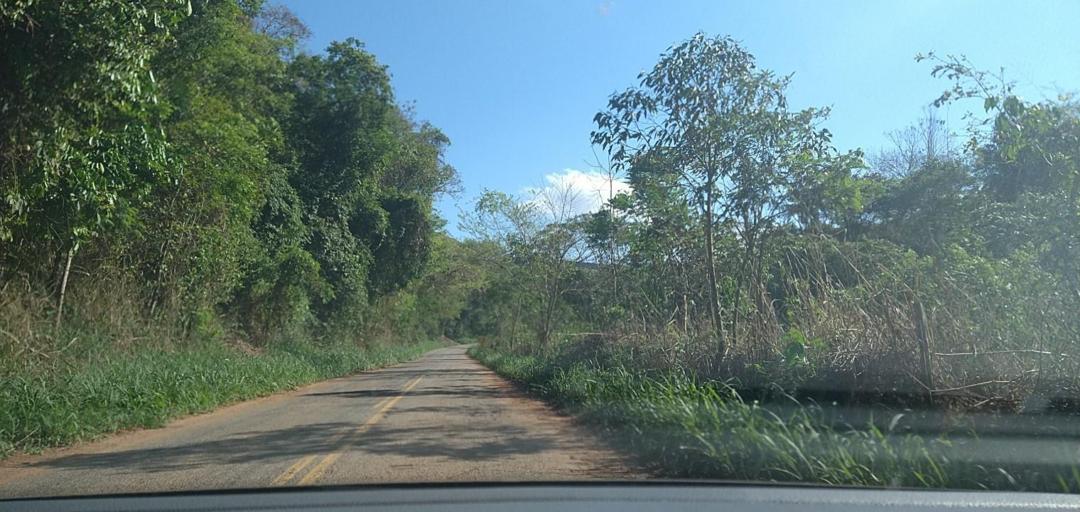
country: BR
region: Minas Gerais
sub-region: Alvinopolis
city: Alvinopolis
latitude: -20.1791
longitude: -42.9310
